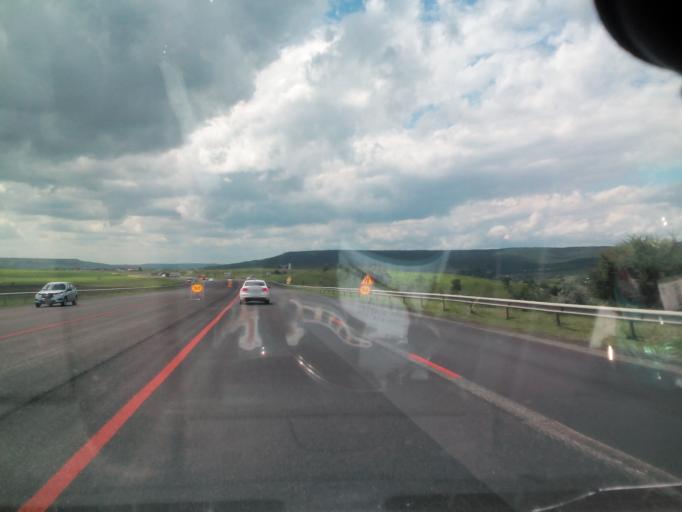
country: RU
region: Stavropol'skiy
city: Tatarka
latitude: 44.9511
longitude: 41.9416
